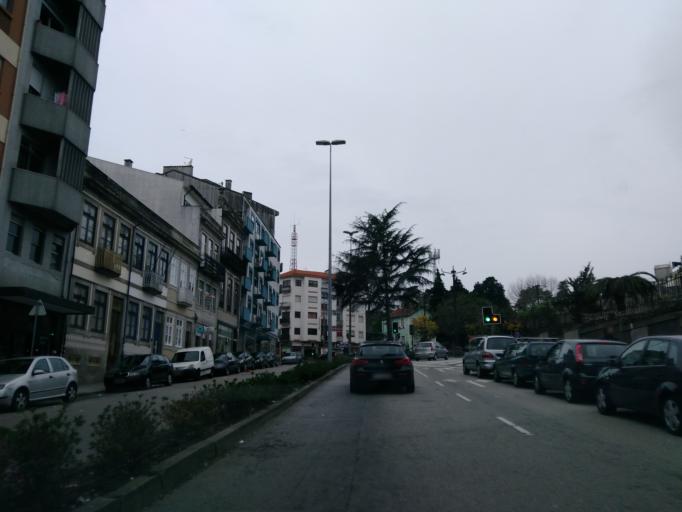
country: PT
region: Porto
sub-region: Porto
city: Porto
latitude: 41.1507
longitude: -8.5931
